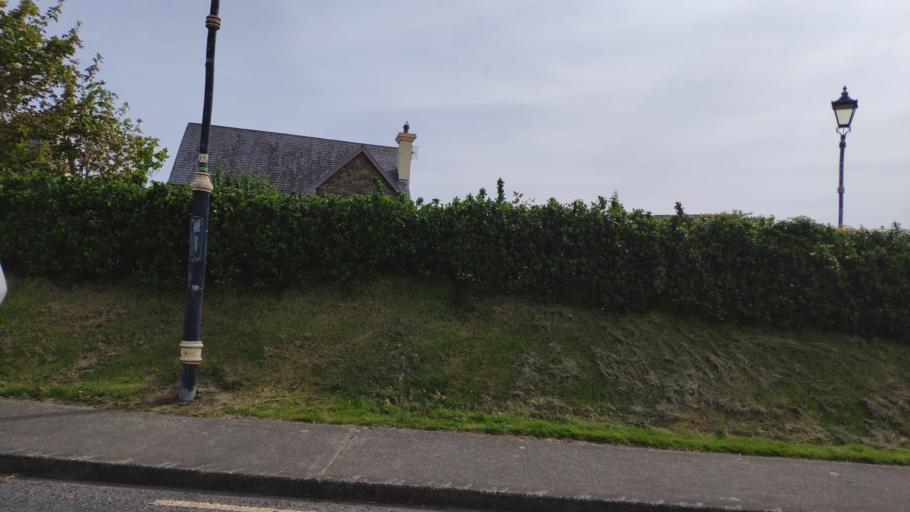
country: IE
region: Munster
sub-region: County Cork
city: Blarney
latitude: 51.9787
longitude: -8.5135
